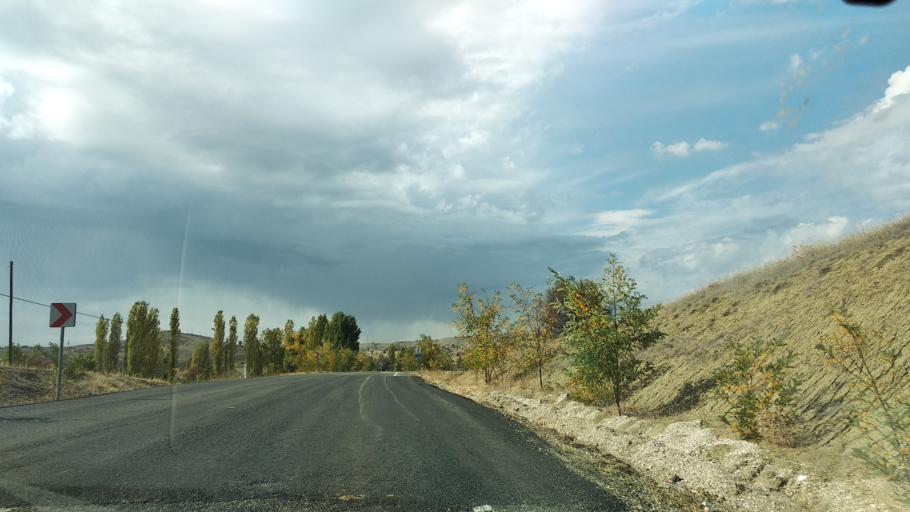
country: TR
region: Bolu
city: Seben
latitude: 40.3844
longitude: 31.5343
